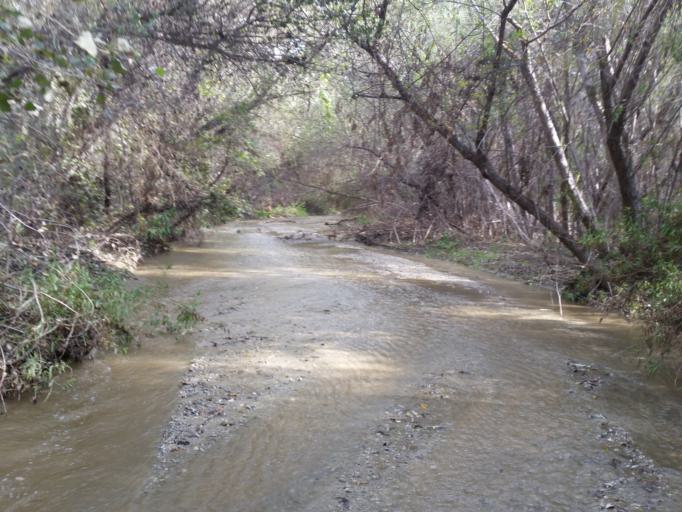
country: US
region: California
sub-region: San Bernardino County
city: Redlands
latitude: 34.0209
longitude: -117.1861
